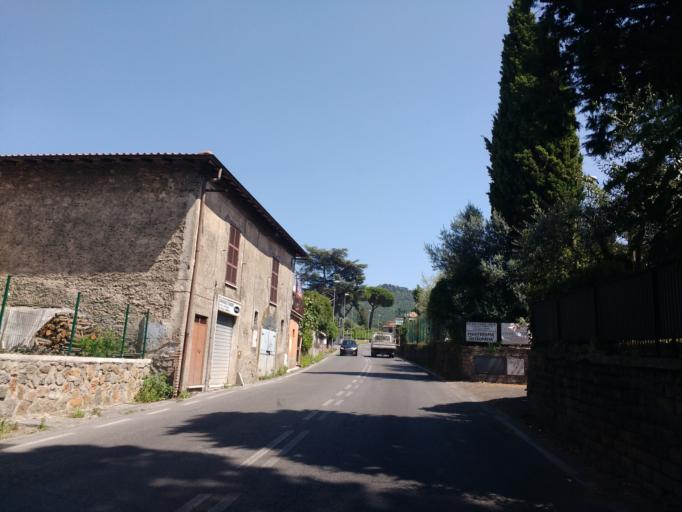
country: IT
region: Latium
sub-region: Citta metropolitana di Roma Capitale
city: Rocca di Papa
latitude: 41.7744
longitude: 12.6973
